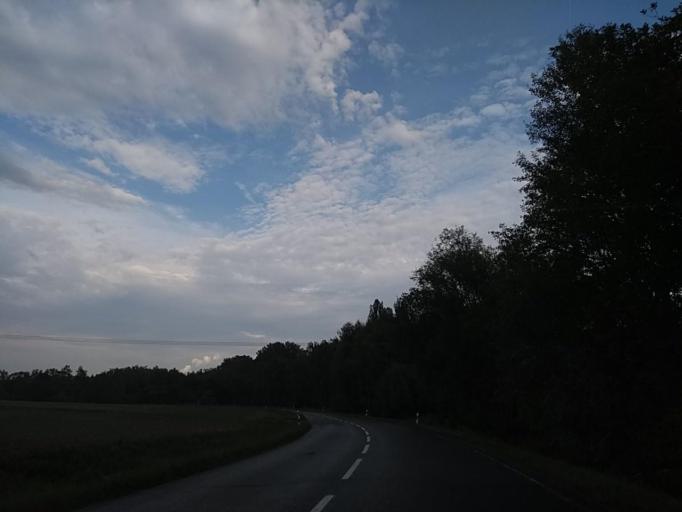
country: DE
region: Saxony-Anhalt
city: Hohenmolsen
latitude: 51.1588
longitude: 12.1160
